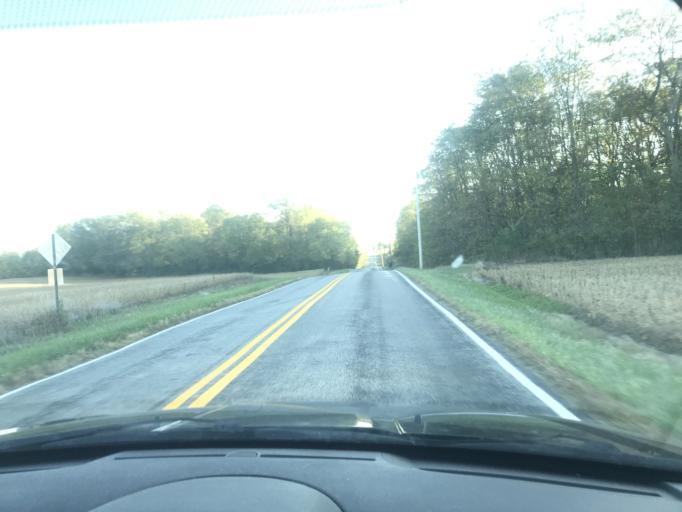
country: US
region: Ohio
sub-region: Logan County
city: De Graff
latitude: 40.2385
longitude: -83.8629
